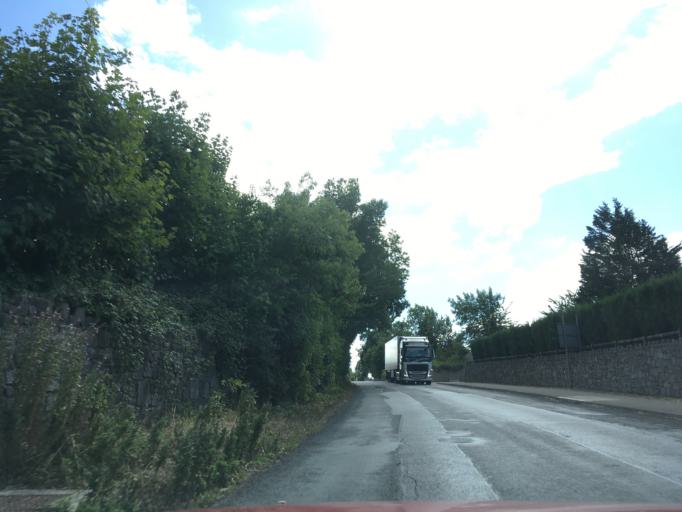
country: IE
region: Munster
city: Cahir
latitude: 52.3642
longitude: -7.9335
